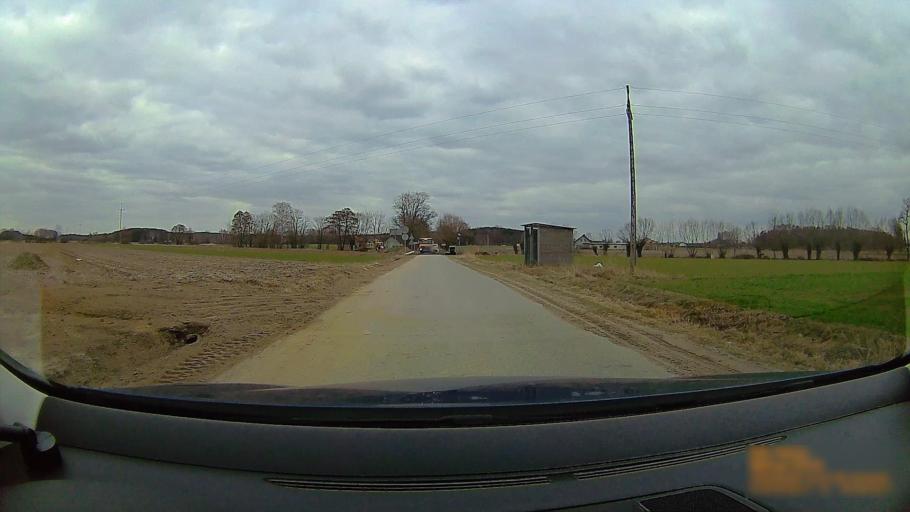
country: PL
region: Greater Poland Voivodeship
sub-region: Powiat koninski
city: Rzgow Pierwszy
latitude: 52.1289
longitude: 18.0707
